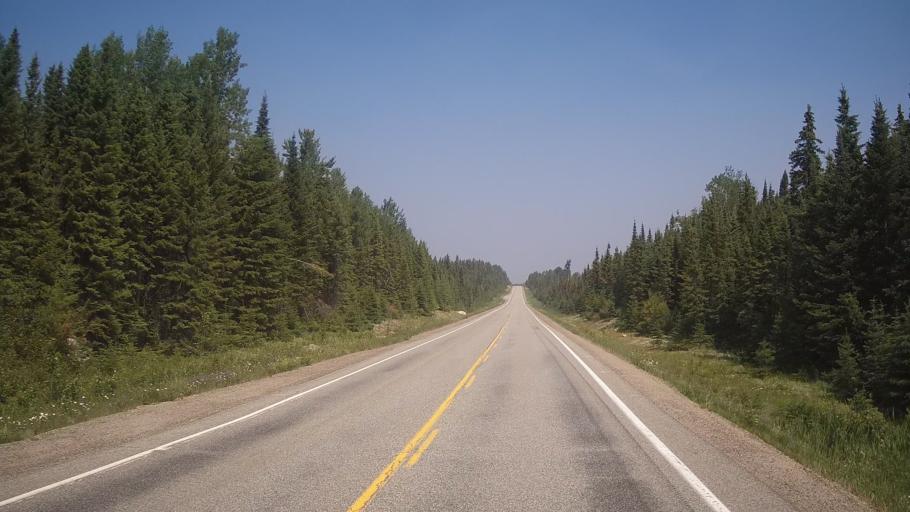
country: CA
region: Ontario
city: Timmins
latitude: 48.1746
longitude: -81.5821
